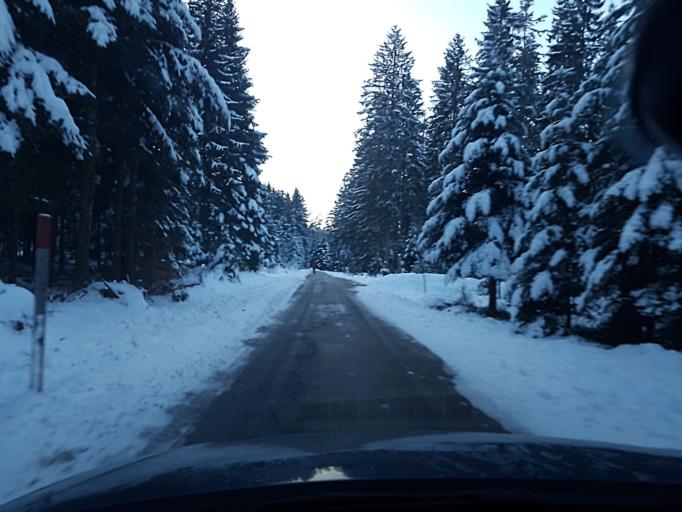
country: DE
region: Baden-Wuerttemberg
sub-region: Freiburg Region
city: Unterkirnach
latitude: 48.0973
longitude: 8.3627
